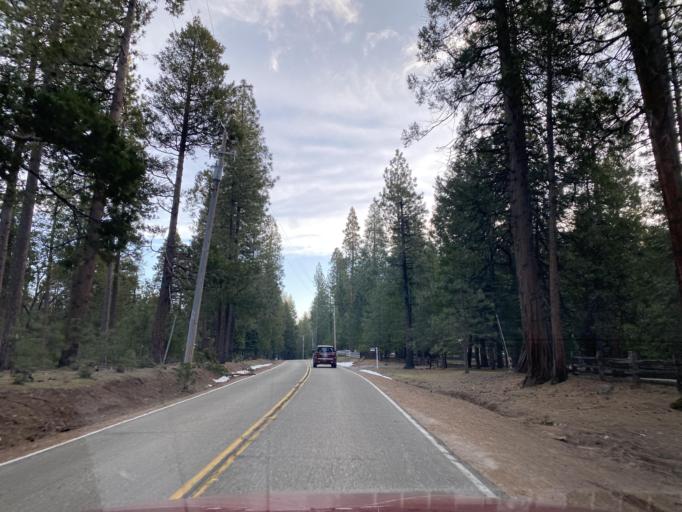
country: US
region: California
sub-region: Amador County
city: Pioneer
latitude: 38.5002
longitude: -120.5544
